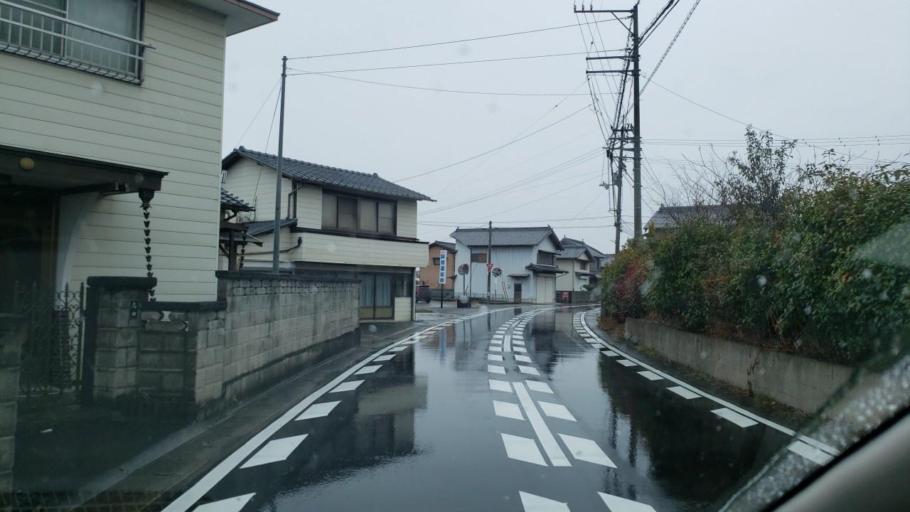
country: JP
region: Tokushima
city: Kamojimacho-jogejima
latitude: 34.1000
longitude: 134.3955
